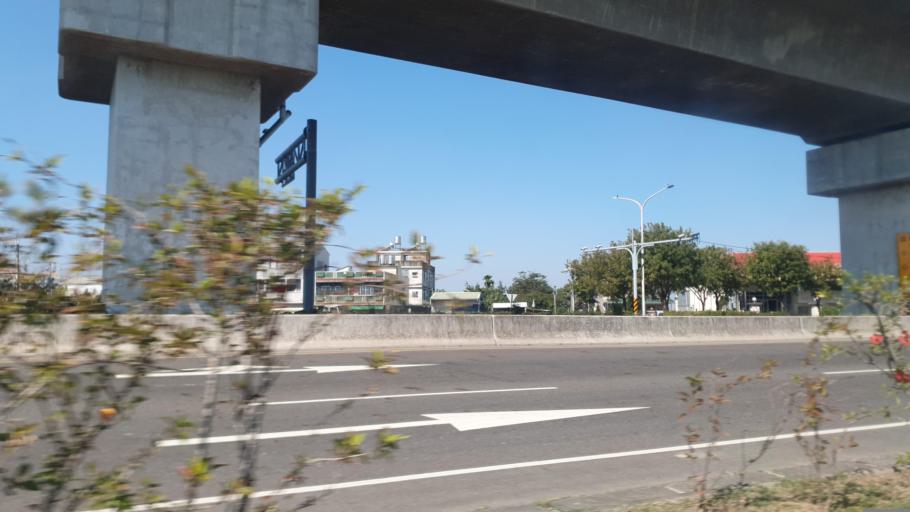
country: TW
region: Taiwan
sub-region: Tainan
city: Tainan
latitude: 23.0223
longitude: 120.2894
